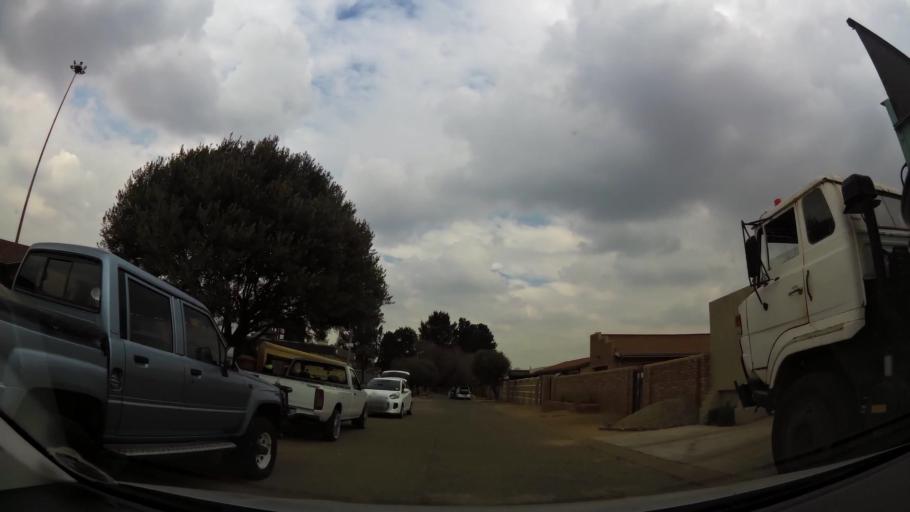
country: ZA
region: Gauteng
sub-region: City of Johannesburg Metropolitan Municipality
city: Soweto
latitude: -26.2649
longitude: 27.8625
